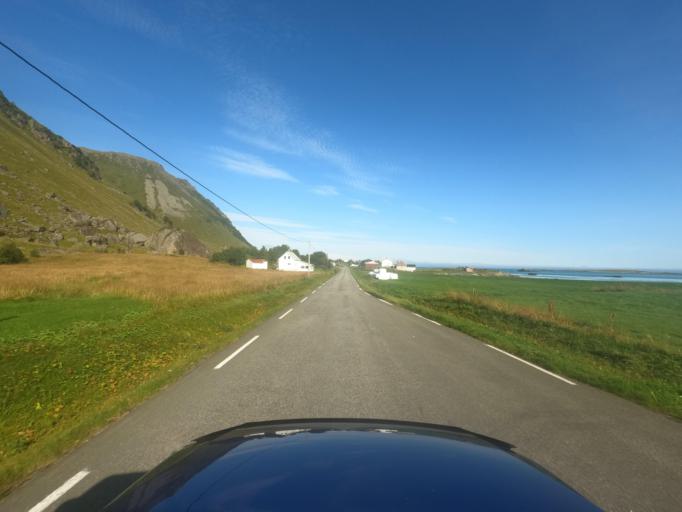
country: NO
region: Nordland
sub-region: Vestvagoy
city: Evjen
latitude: 68.3151
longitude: 14.0150
